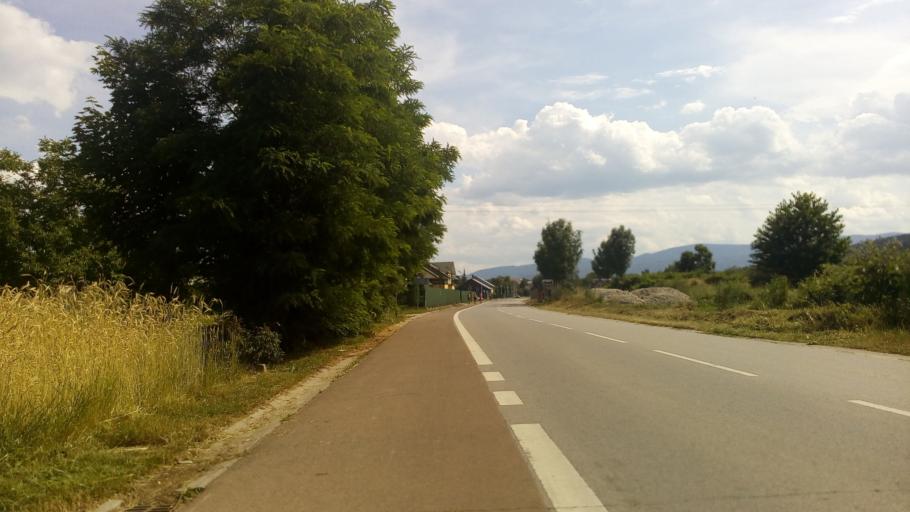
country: PL
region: Lesser Poland Voivodeship
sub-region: Powiat nowosadecki
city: Stary Sacz
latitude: 49.5738
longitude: 20.6362
